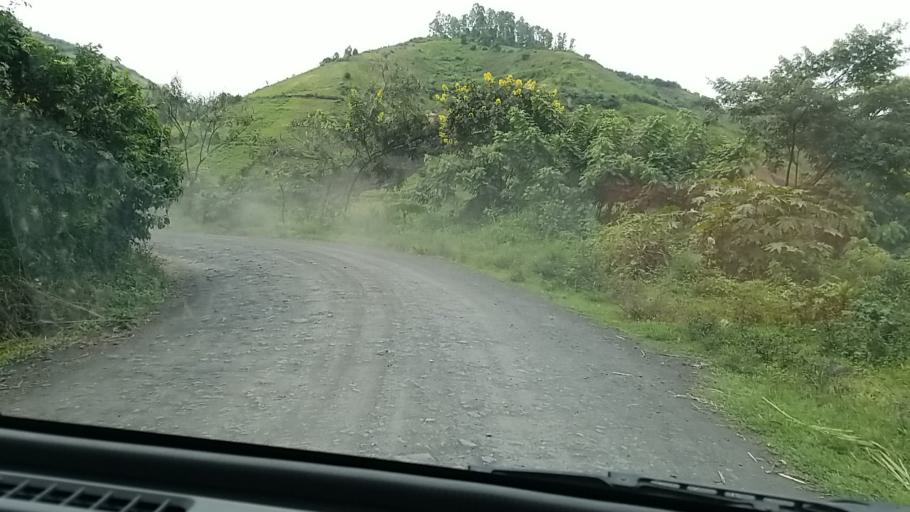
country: CD
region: Nord Kivu
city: Sake
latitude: -1.7427
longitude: 28.9930
